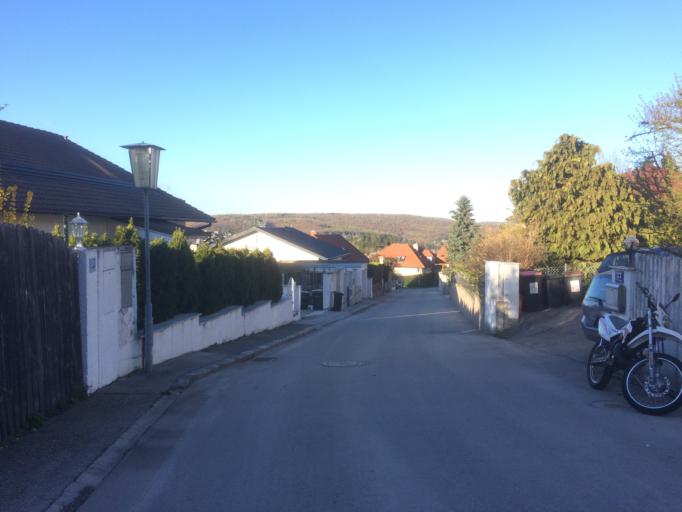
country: AT
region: Lower Austria
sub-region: Politischer Bezirk Wien-Umgebung
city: Gablitz
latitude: 48.2186
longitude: 16.1403
